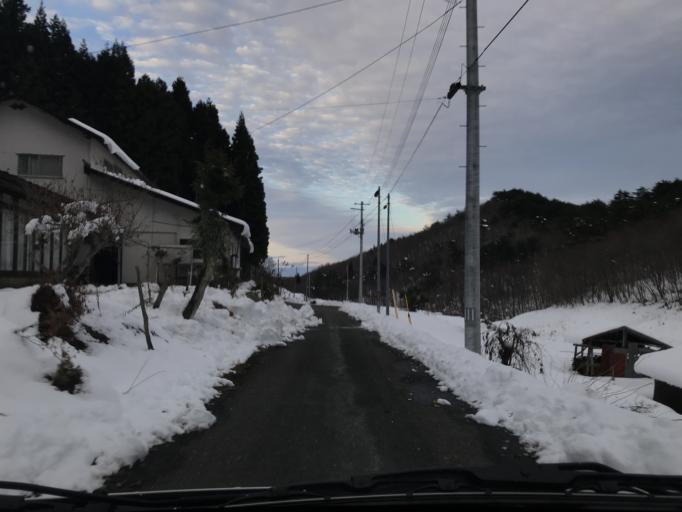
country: JP
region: Iwate
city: Mizusawa
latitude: 39.0396
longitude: 141.0188
